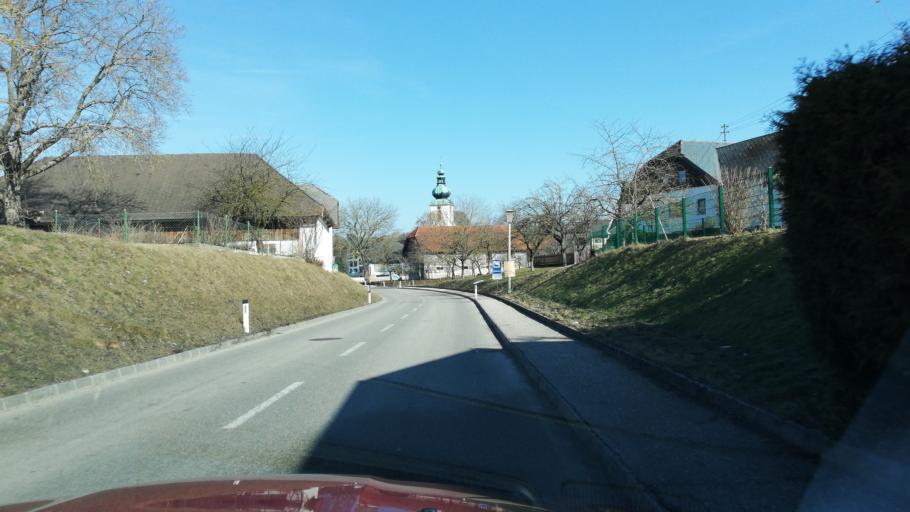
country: AT
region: Upper Austria
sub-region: Politischer Bezirk Vocklabruck
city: Desselbrunn
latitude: 48.0210
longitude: 13.7704
